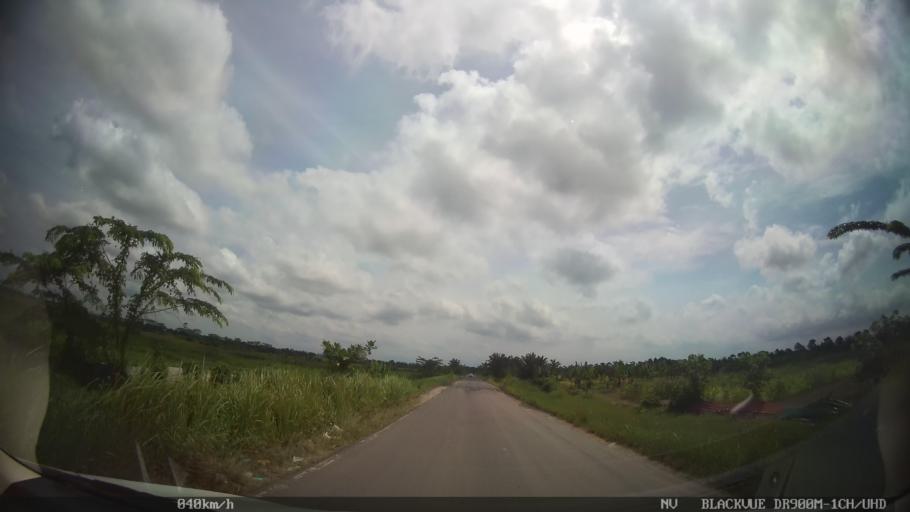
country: ID
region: North Sumatra
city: Percut
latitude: 3.6054
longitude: 98.8408
